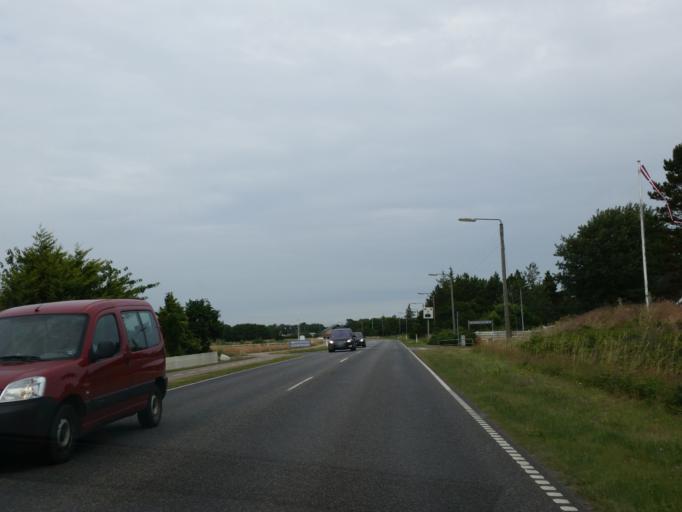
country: DE
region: Schleswig-Holstein
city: List
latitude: 55.1256
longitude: 8.5496
